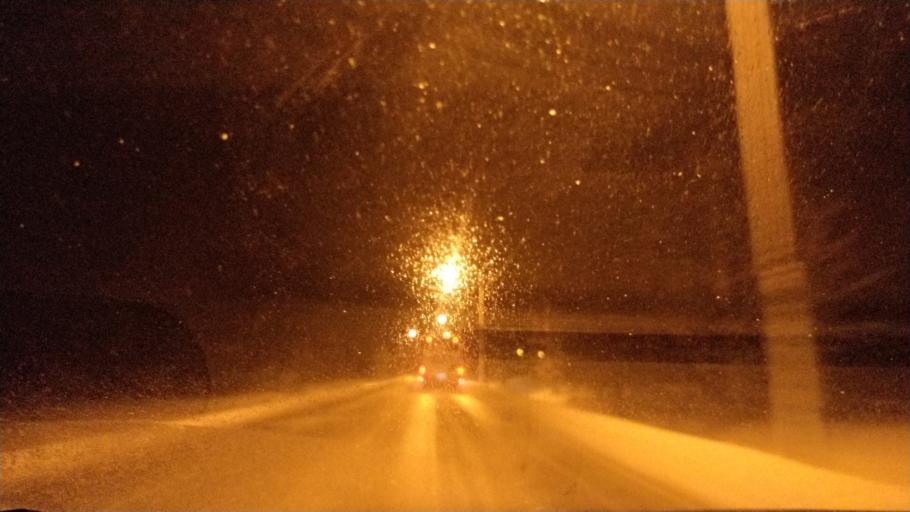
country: FI
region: Lapland
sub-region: Rovaniemi
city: Rovaniemi
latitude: 66.2933
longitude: 25.3506
